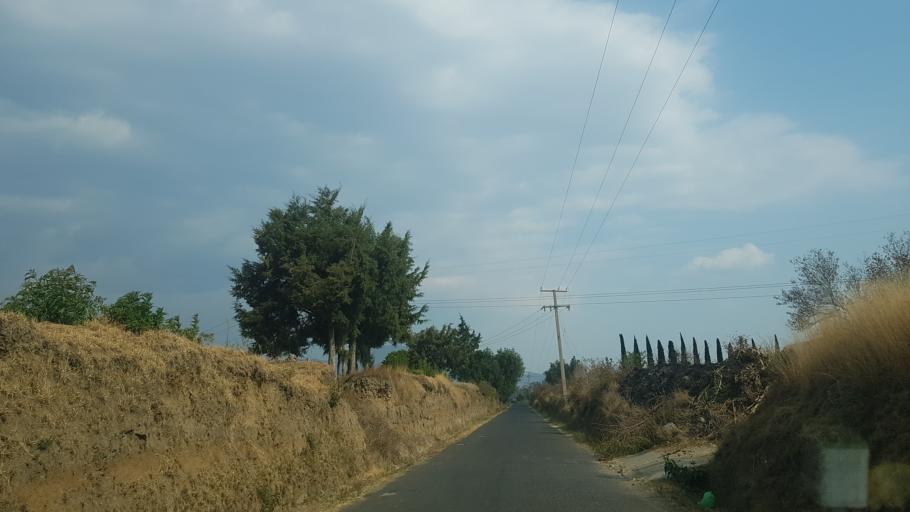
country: MX
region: Puebla
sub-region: Santa Isabel Cholula
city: Santa Ana Acozautla
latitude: 18.9536
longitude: -98.3993
